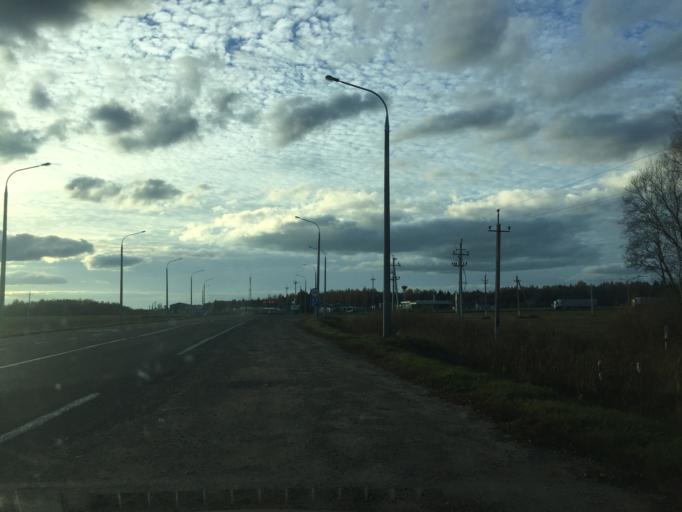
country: BY
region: Vitebsk
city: Druya
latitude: 55.8202
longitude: 27.6412
